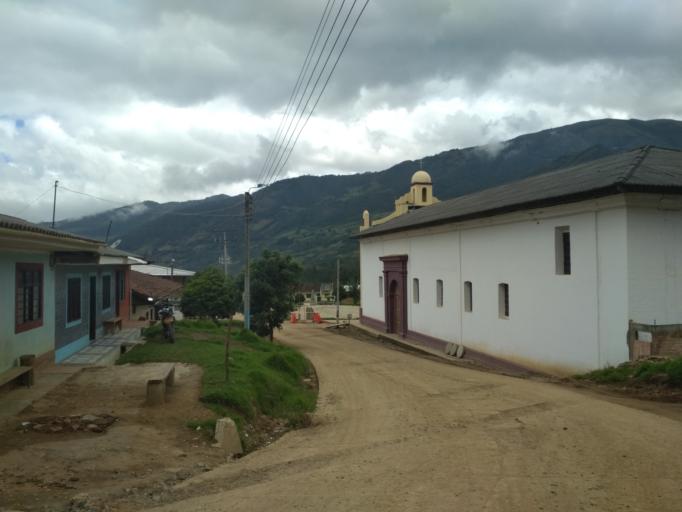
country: CO
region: Cauca
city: Jambalo
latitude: 2.7123
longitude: -76.3250
